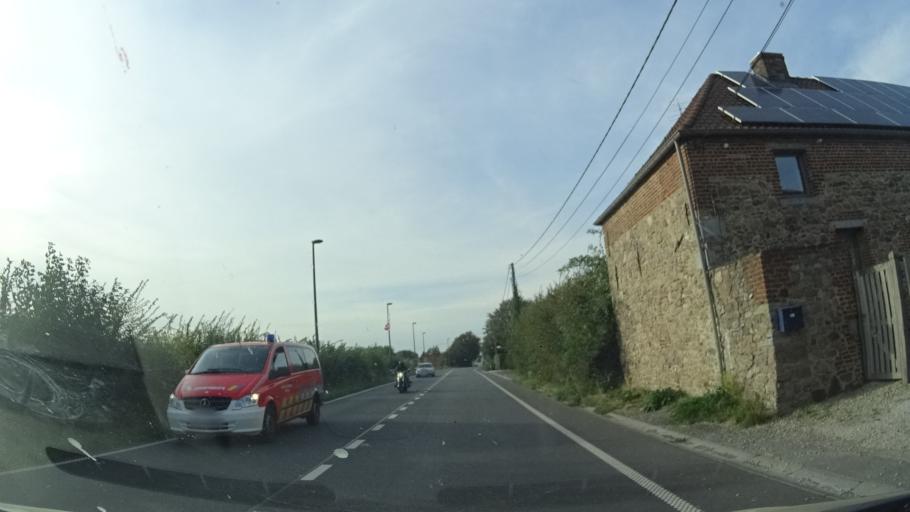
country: FR
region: Nord-Pas-de-Calais
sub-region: Departement du Nord
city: Marpent
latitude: 50.3569
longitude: 4.0603
